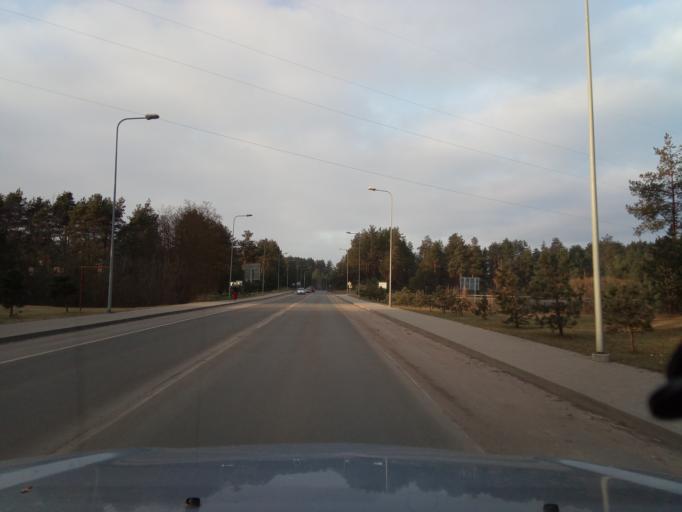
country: LT
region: Alytaus apskritis
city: Varena
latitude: 54.2194
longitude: 24.5603
